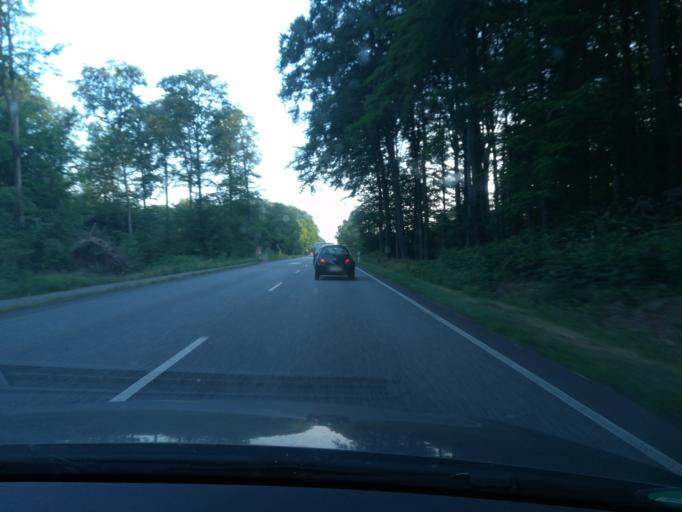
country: DE
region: Schleswig-Holstein
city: Kasseburg
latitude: 53.5476
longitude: 10.4183
